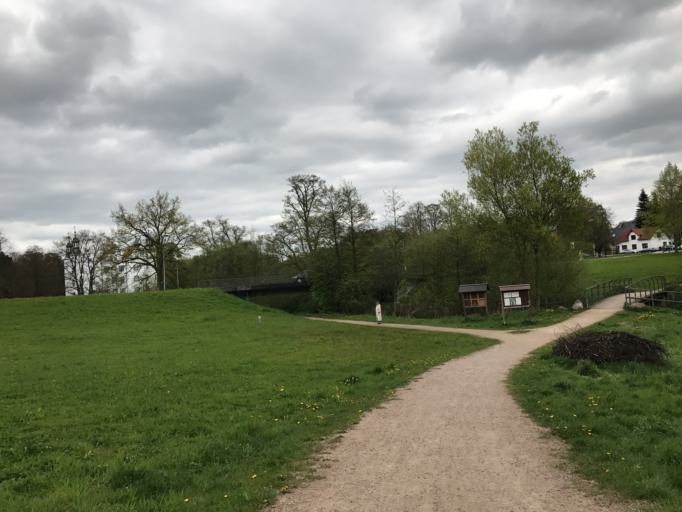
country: DE
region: Schleswig-Holstein
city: Ahrensburg
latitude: 53.6782
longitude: 10.2417
